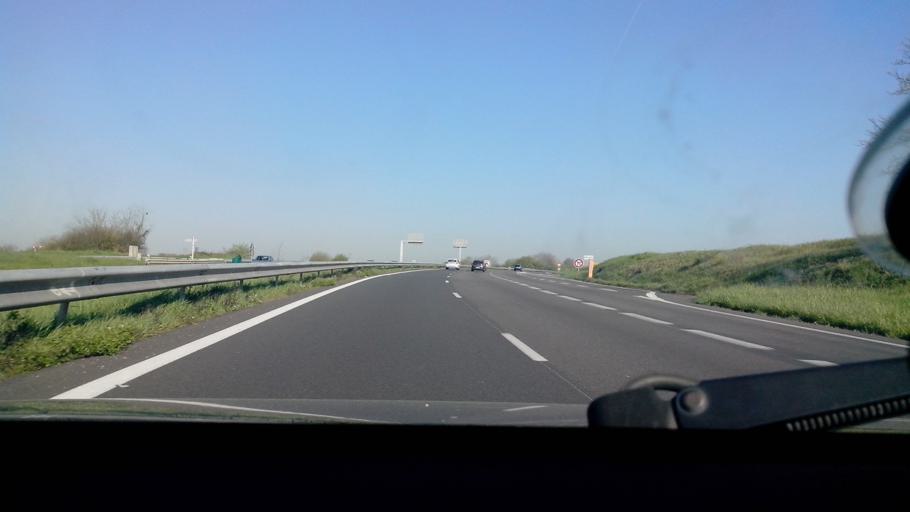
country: FR
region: Ile-de-France
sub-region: Departement de l'Essonne
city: Bures-sur-Yvette
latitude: 48.7154
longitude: 2.1736
